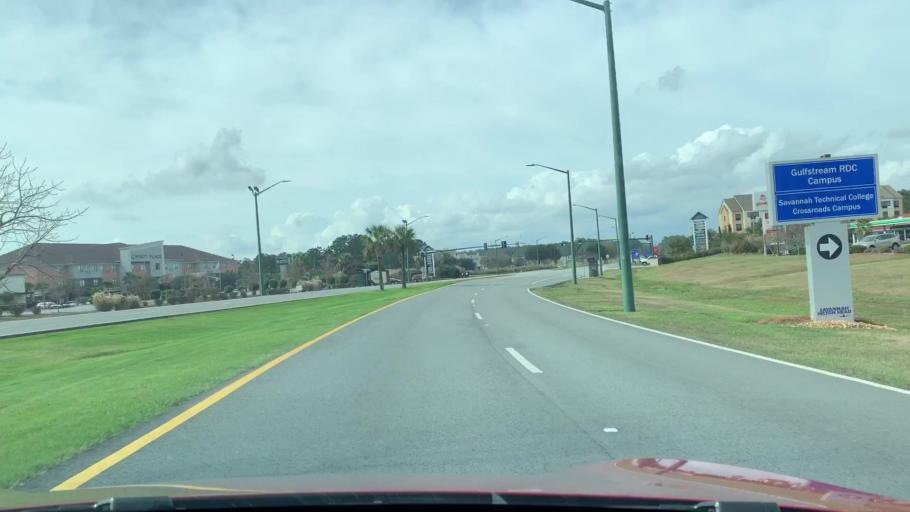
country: US
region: Georgia
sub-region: Chatham County
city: Pooler
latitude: 32.1384
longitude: -81.2321
